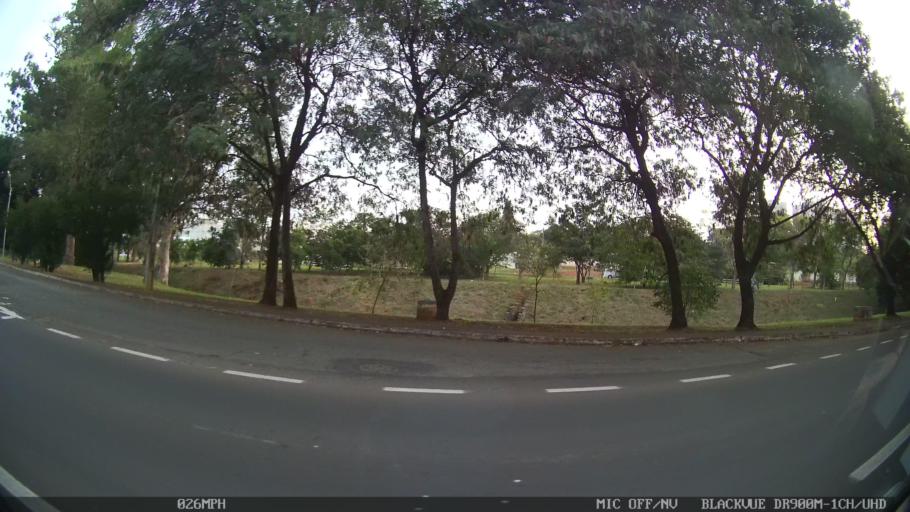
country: BR
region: Sao Paulo
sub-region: Limeira
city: Limeira
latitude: -22.5645
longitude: -47.4166
